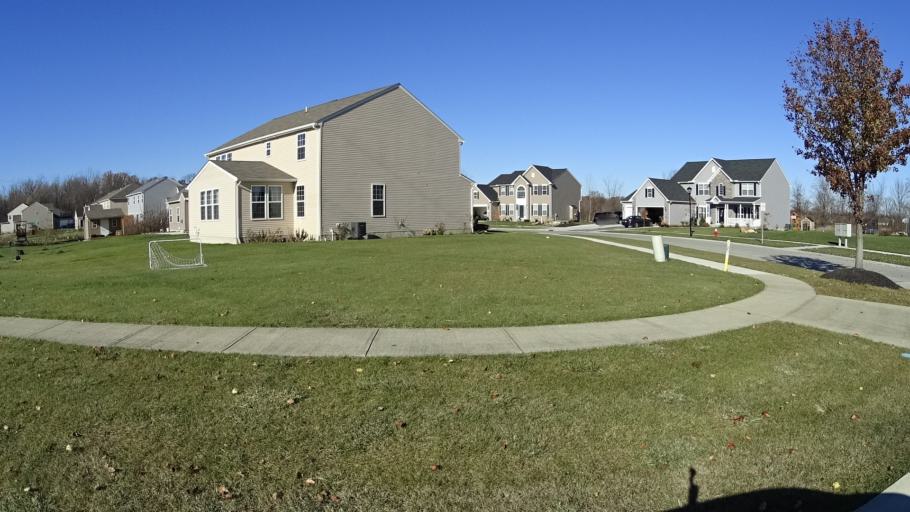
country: US
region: Ohio
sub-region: Lorain County
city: Avon
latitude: 41.4391
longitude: -82.0614
